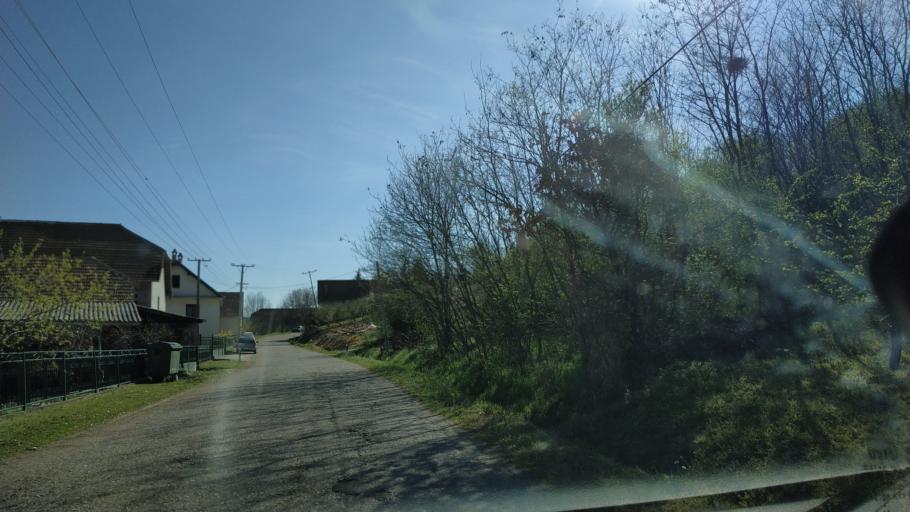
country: RS
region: Central Serbia
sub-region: Nisavski Okrug
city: Aleksinac
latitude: 43.4863
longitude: 21.6593
